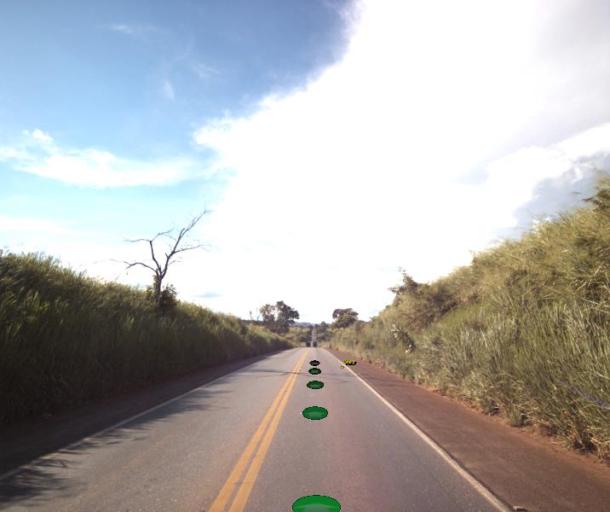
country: BR
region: Goias
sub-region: Rialma
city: Rialma
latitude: -15.3394
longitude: -49.5695
